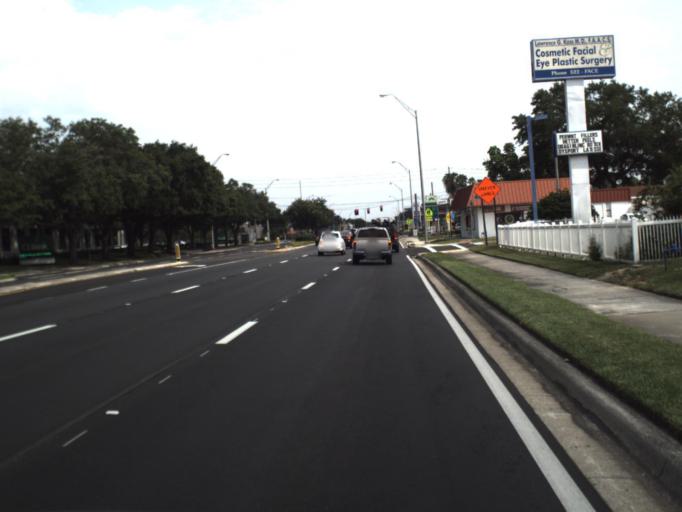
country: US
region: Florida
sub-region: Pinellas County
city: Lealman
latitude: 27.8263
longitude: -82.6385
